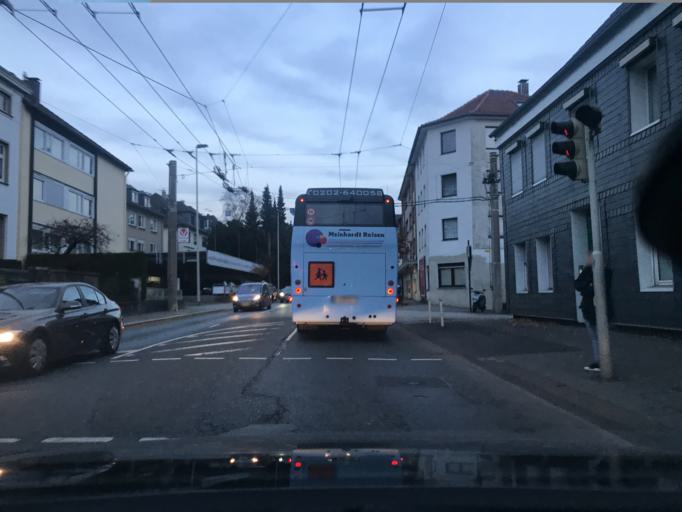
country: DE
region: North Rhine-Westphalia
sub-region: Regierungsbezirk Dusseldorf
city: Solingen
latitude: 51.1773
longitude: 7.0752
